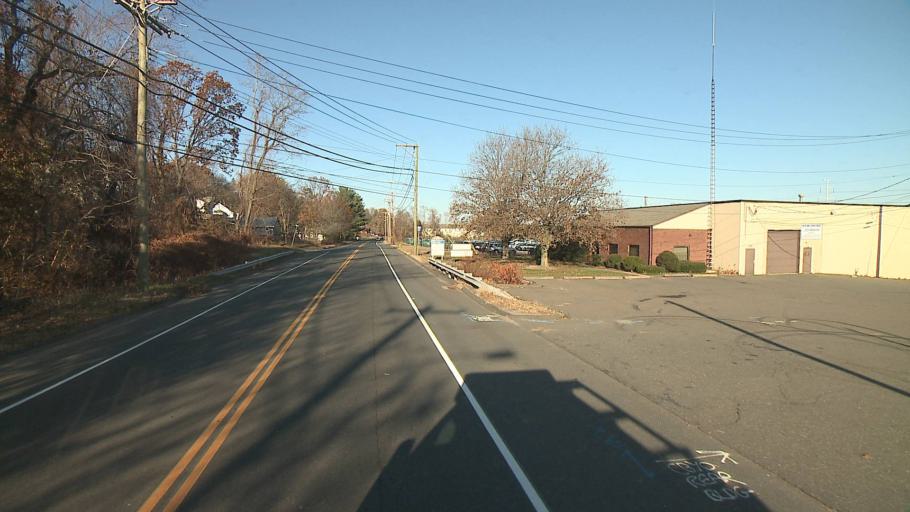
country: US
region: Connecticut
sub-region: New Haven County
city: Hamden
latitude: 41.3565
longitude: -72.8905
